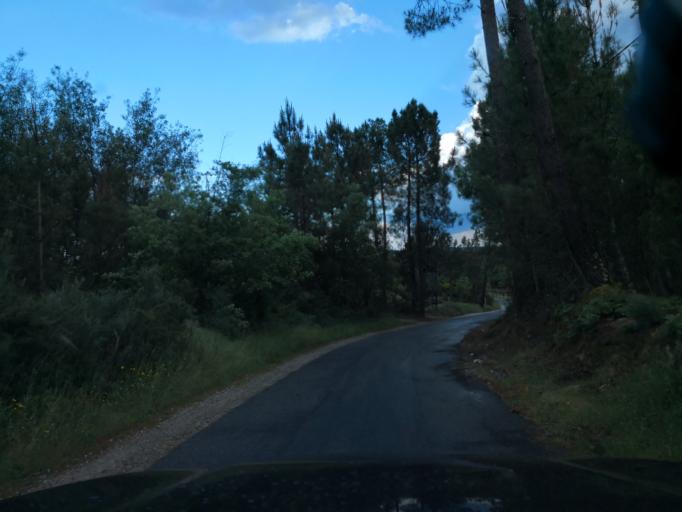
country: PT
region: Vila Real
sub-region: Vila Real
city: Vila Real
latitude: 41.3528
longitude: -7.7261
